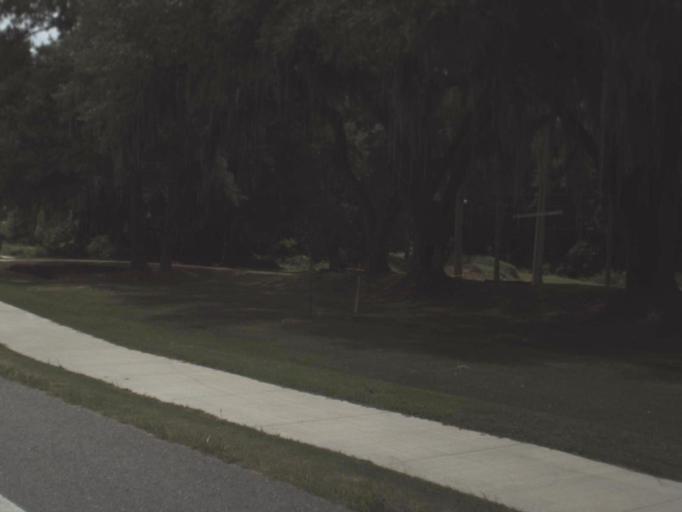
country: US
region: Florida
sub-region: Madison County
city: Madison
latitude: 30.4761
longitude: -83.4355
